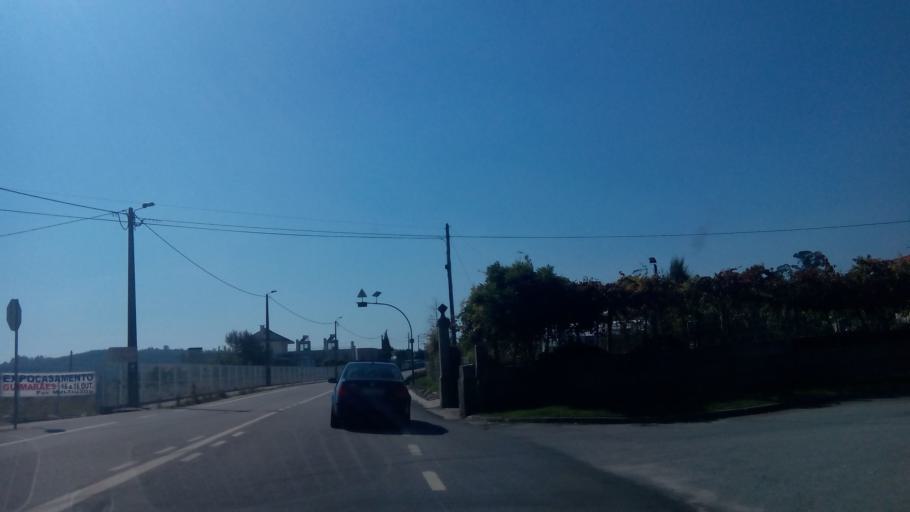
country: PT
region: Porto
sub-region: Lousada
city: Meinedo
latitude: 41.2223
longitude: -8.2398
